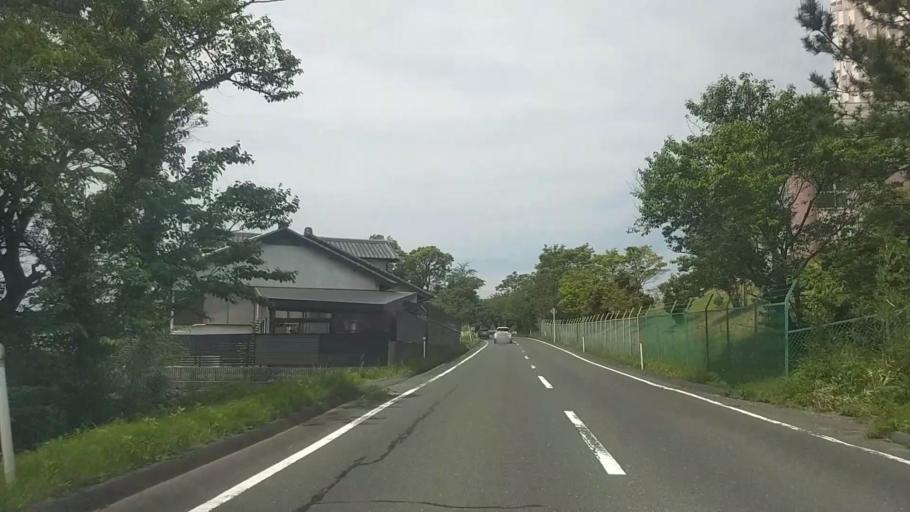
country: JP
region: Shizuoka
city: Kosai-shi
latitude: 34.7828
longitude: 137.5752
